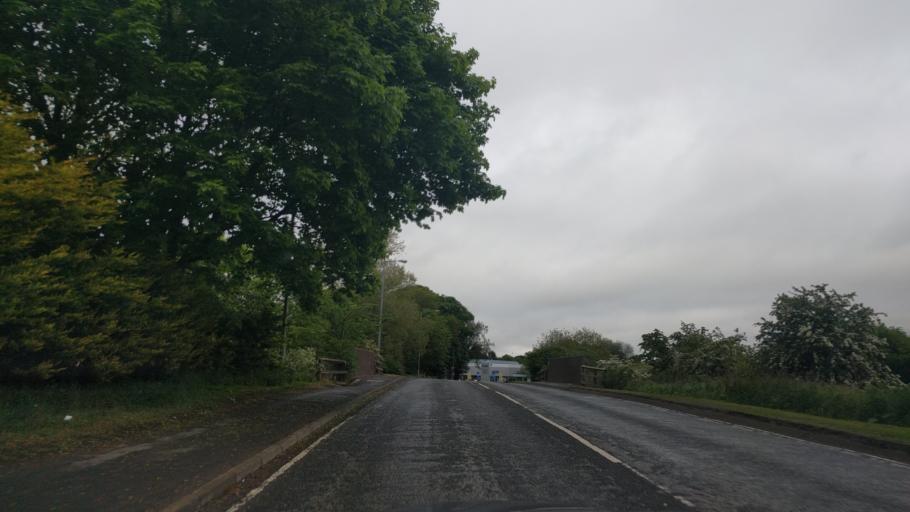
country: GB
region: England
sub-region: Northumberland
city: Morpeth
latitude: 55.1592
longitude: -1.6688
